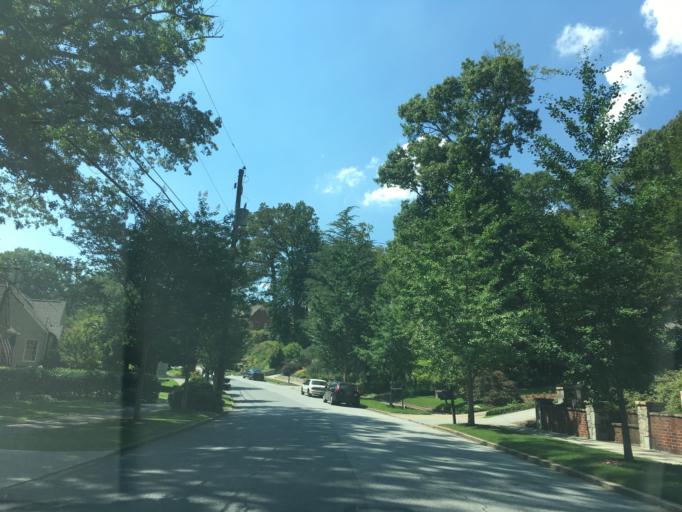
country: US
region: Georgia
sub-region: DeKalb County
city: Druid Hills
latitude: 33.8014
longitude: -84.3620
